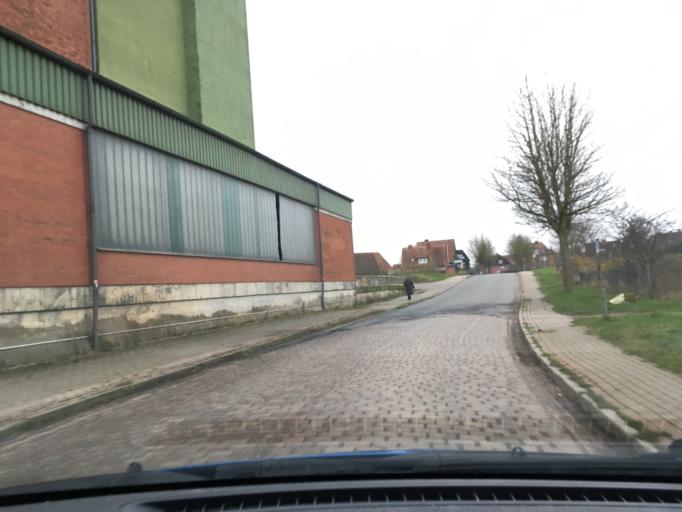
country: DE
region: Lower Saxony
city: Bleckede
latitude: 53.2935
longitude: 10.7354
